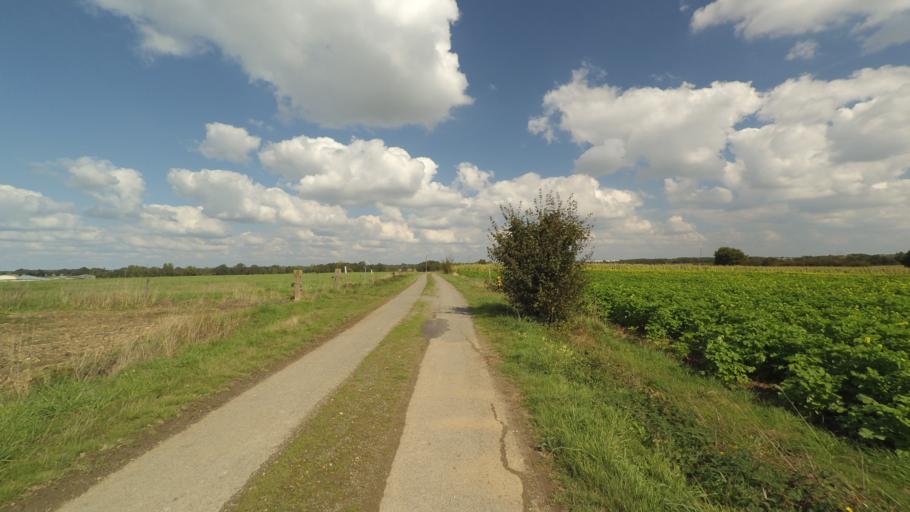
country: FR
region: Pays de la Loire
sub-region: Departement de la Vendee
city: Bouffere
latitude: 46.9573
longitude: -1.3723
